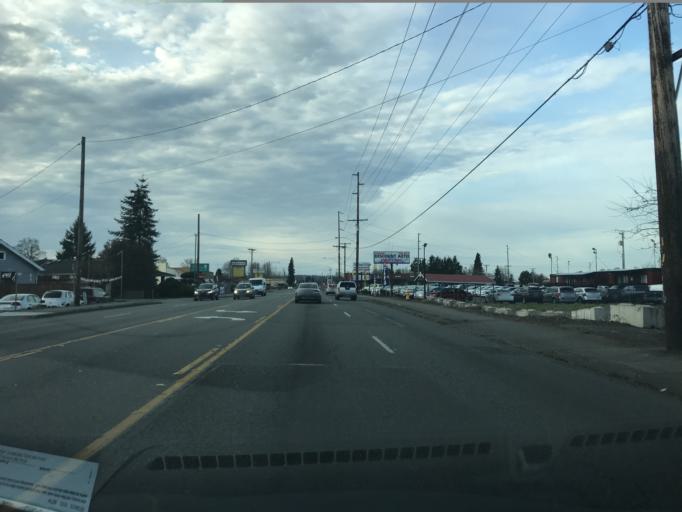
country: US
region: Washington
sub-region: King County
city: Kent
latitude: 47.3483
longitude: -122.2239
